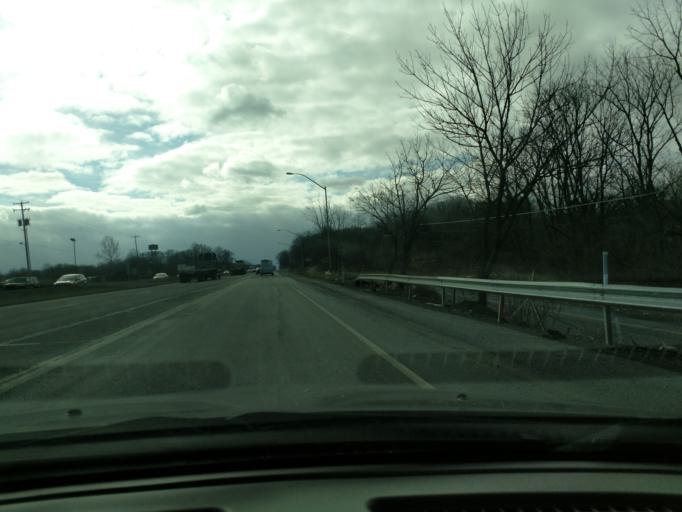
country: US
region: Pennsylvania
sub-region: Schuylkill County
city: Lake Wynonah
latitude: 40.5155
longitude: -76.1135
